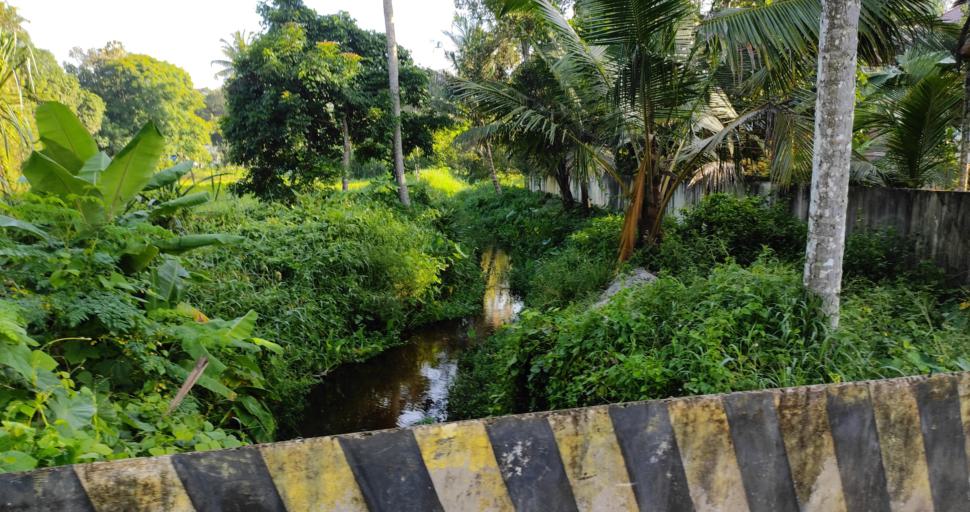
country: IN
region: Kerala
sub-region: Alappuzha
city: Shertallai
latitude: 9.6474
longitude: 76.3404
